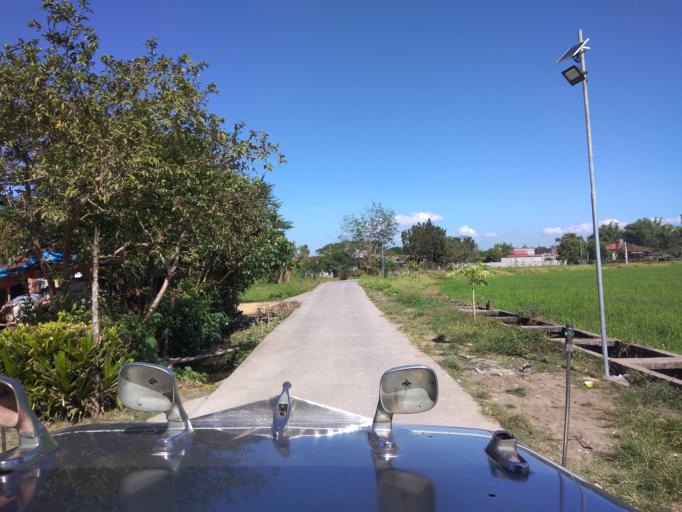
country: PH
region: Central Luzon
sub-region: Province of Pampanga
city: Salapungan
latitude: 15.1553
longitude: 120.9195
